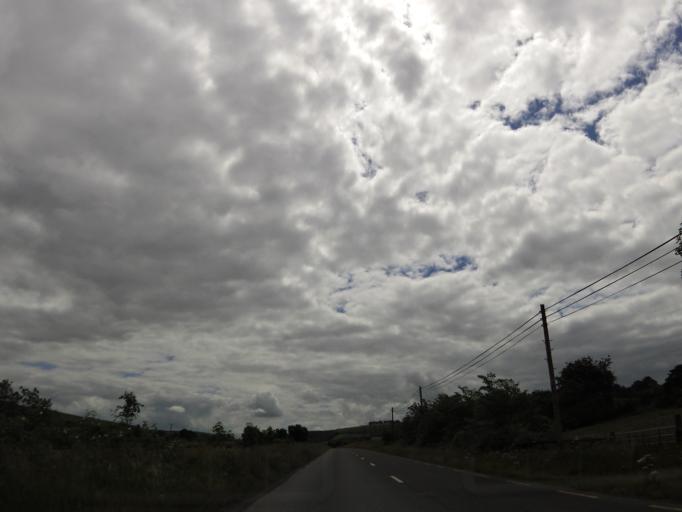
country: IE
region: Munster
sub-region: North Tipperary
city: Templemore
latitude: 52.7656
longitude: -8.0200
